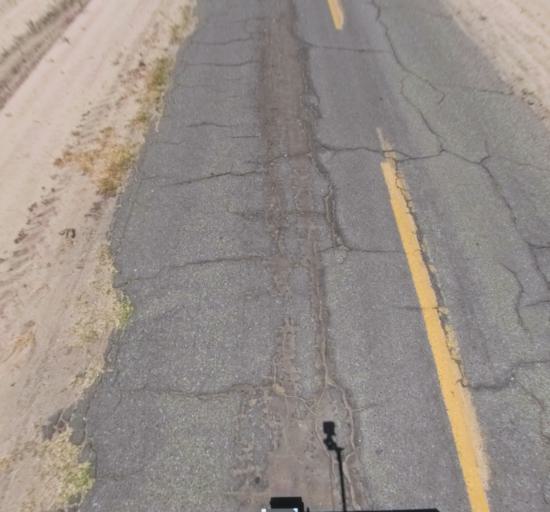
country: US
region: California
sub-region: Madera County
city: Fairmead
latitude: 36.9964
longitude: -120.2152
